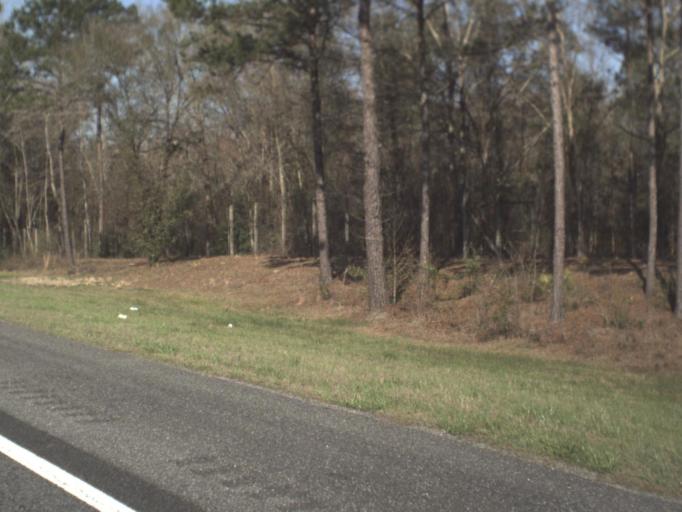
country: US
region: Florida
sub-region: Jefferson County
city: Monticello
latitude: 30.4804
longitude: -84.0557
